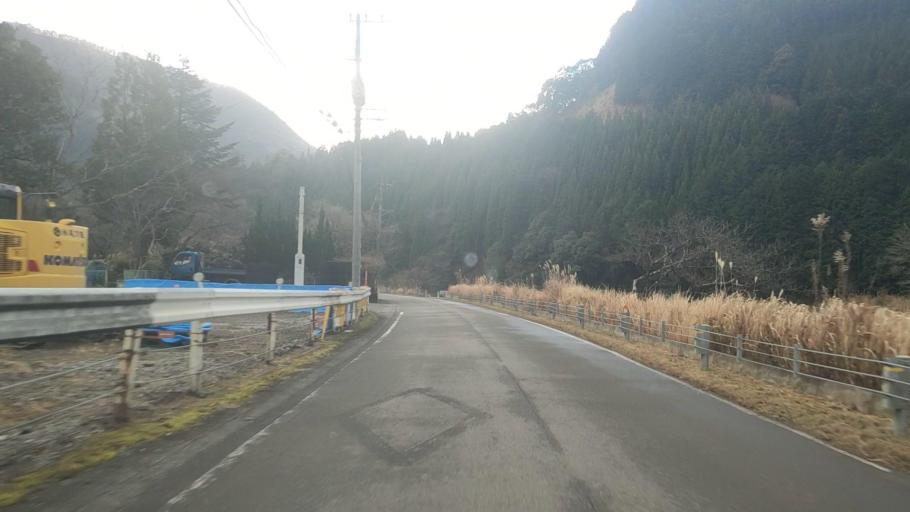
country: JP
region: Kumamoto
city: Hitoyoshi
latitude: 32.4380
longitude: 130.8569
